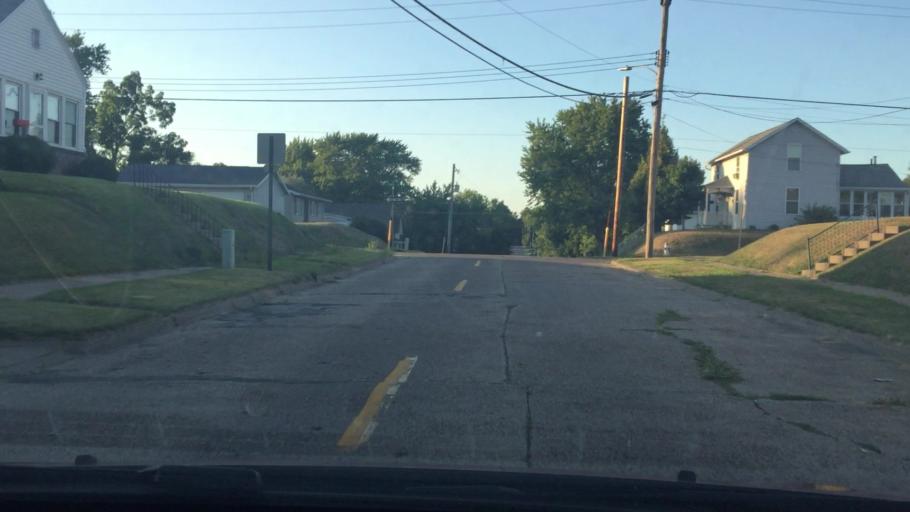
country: US
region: Iowa
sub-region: Muscatine County
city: Muscatine
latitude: 41.4217
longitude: -91.0651
